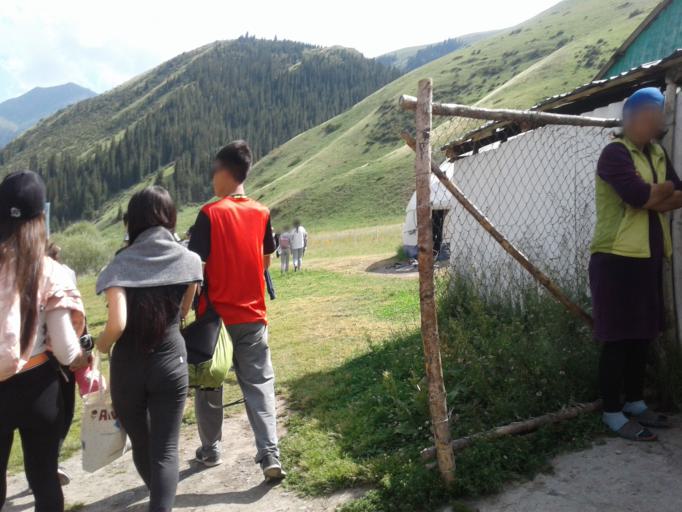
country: KG
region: Naryn
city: Naryn
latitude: 41.4595
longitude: 76.4533
